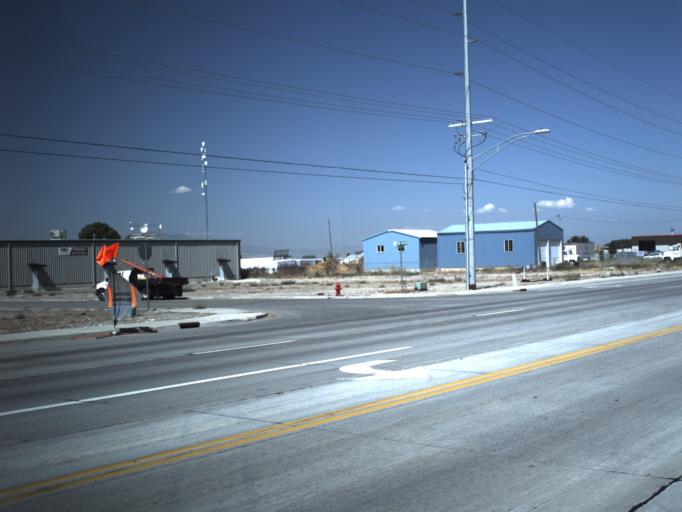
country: US
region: Utah
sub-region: Cache County
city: Logan
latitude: 41.7291
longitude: -111.8598
